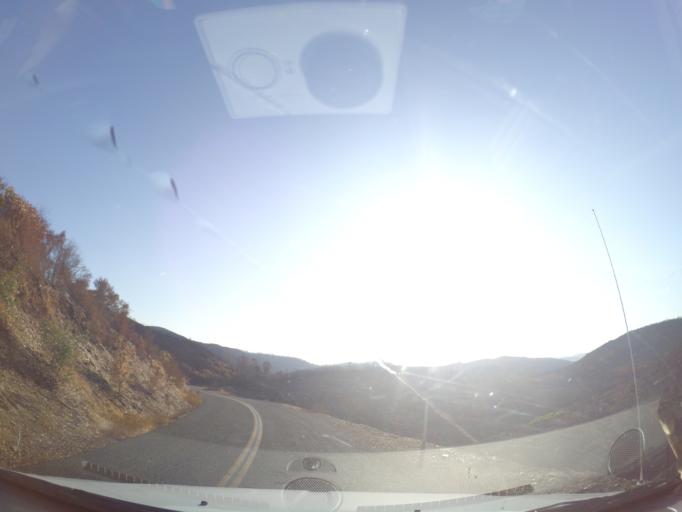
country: US
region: California
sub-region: Mariposa County
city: Mariposa
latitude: 37.5103
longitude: -120.0565
